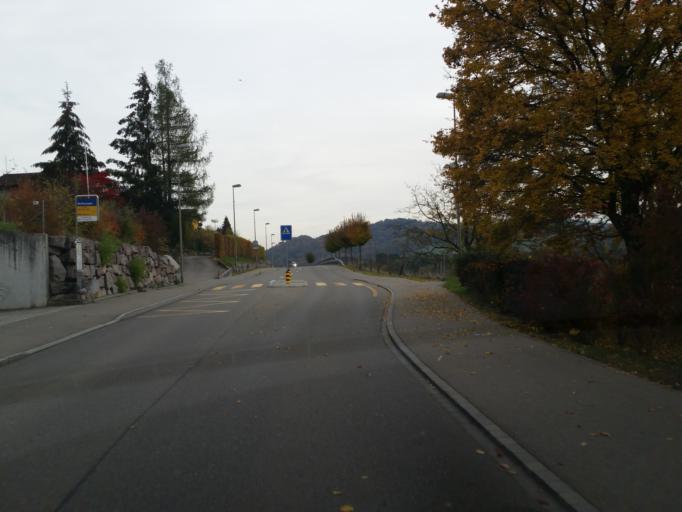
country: CH
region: Zurich
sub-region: Bezirk Winterthur
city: Neftenbach / Dorf Neftenbach
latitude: 47.5218
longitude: 8.6704
